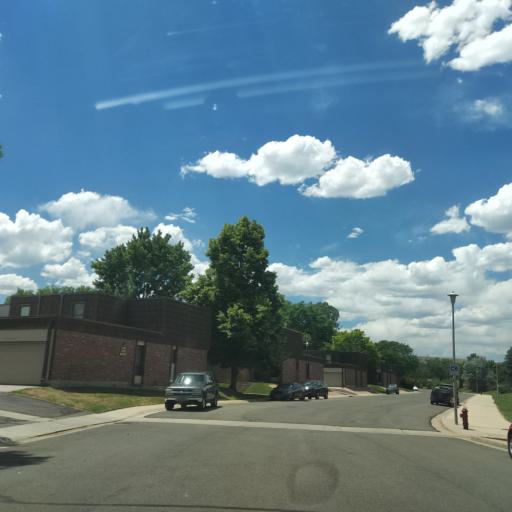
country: US
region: Colorado
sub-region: Jefferson County
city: Lakewood
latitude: 39.6832
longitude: -105.1005
